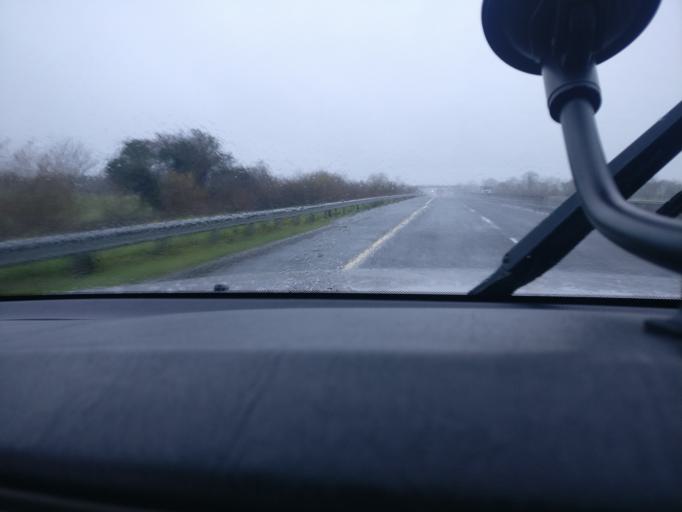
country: IE
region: Leinster
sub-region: An Iarmhi
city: Kilbeggan
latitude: 53.3755
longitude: -7.5530
